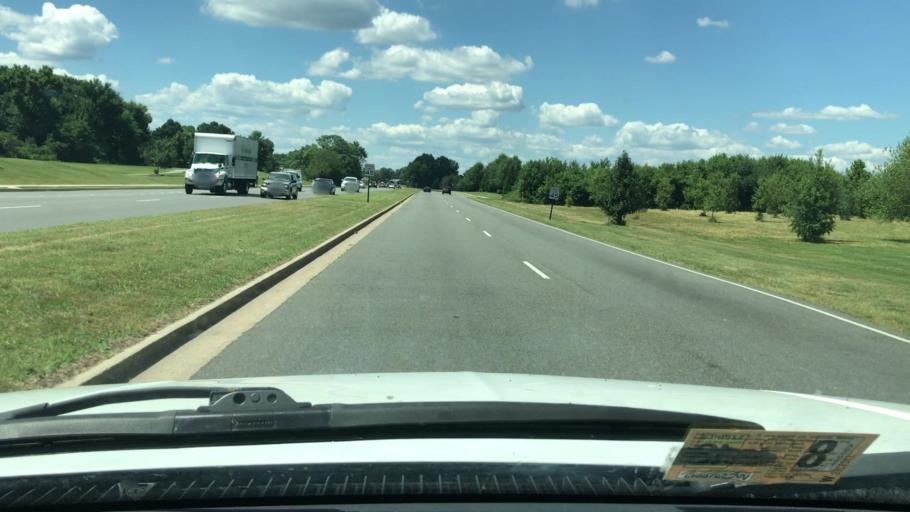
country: US
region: Virginia
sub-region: Henrico County
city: East Highland Park
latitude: 37.5670
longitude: -77.3789
